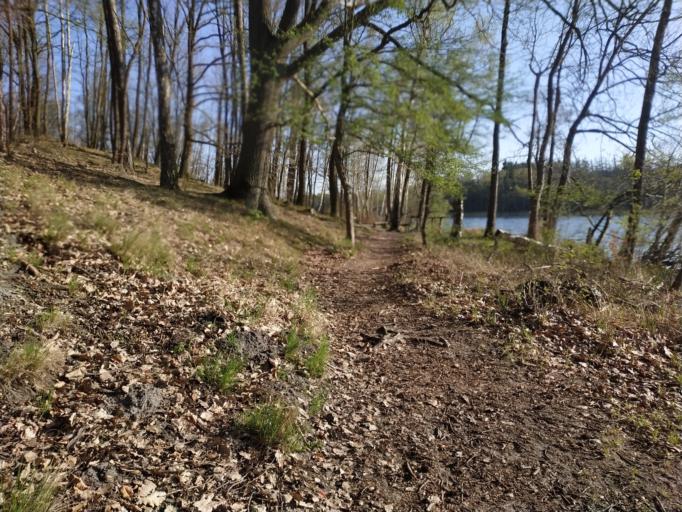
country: DE
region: Brandenburg
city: Strausberg
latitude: 52.5677
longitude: 13.8310
